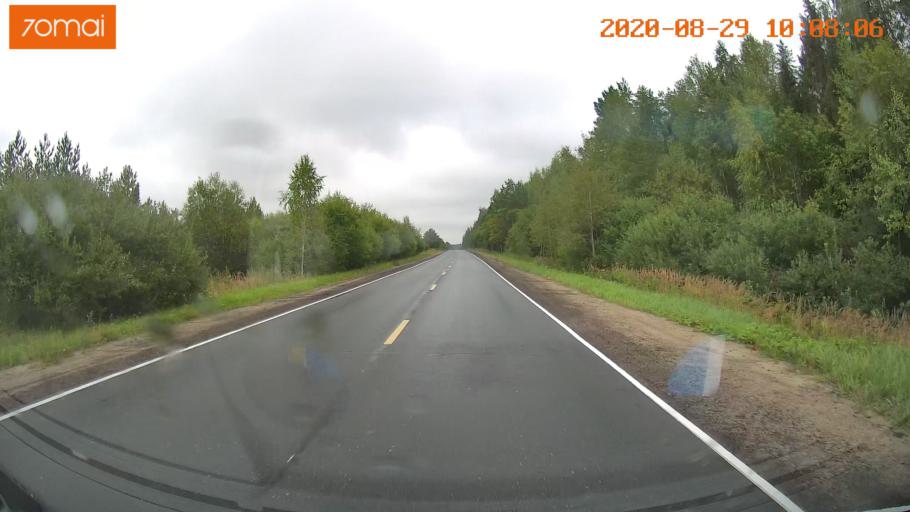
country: RU
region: Ivanovo
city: Kuznechikha
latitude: 57.3771
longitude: 42.5815
